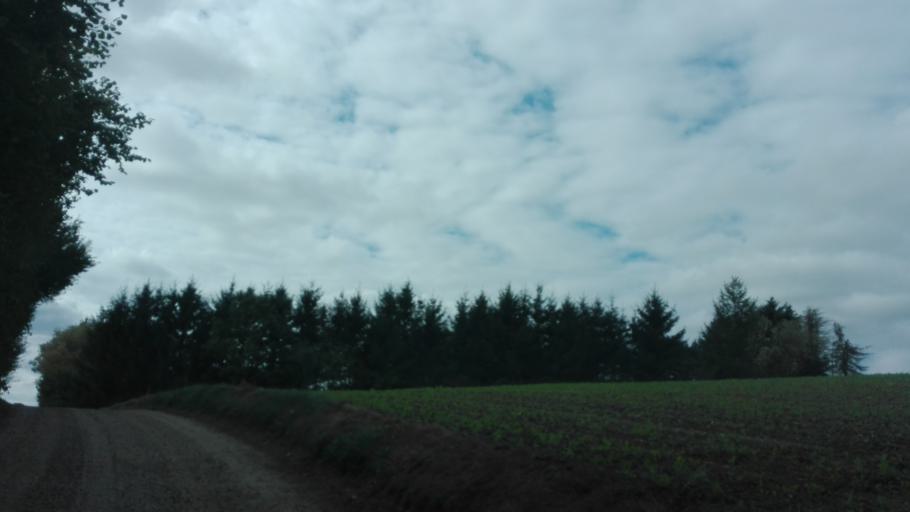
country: DK
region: Central Jutland
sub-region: Skanderborg Kommune
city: Stilling
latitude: 56.0879
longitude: 10.0042
